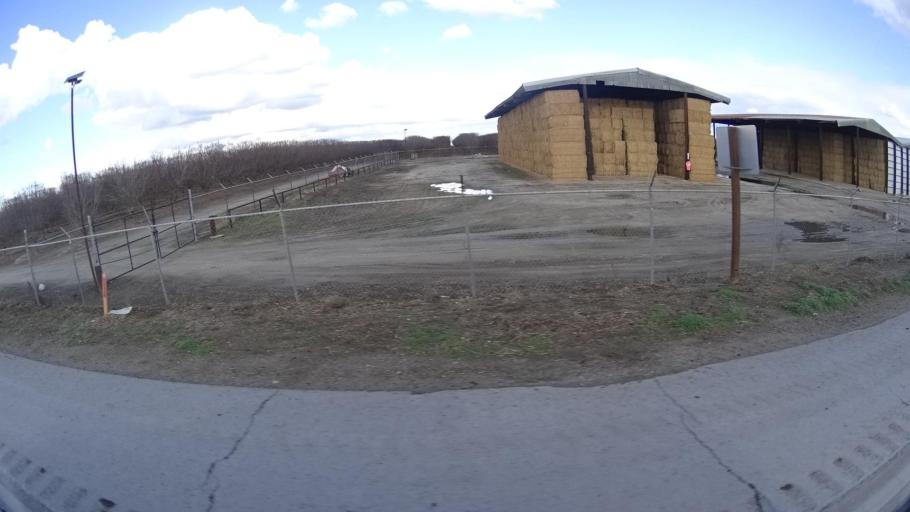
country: US
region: California
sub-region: Kern County
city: Greenfield
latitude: 35.2089
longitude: -119.0997
